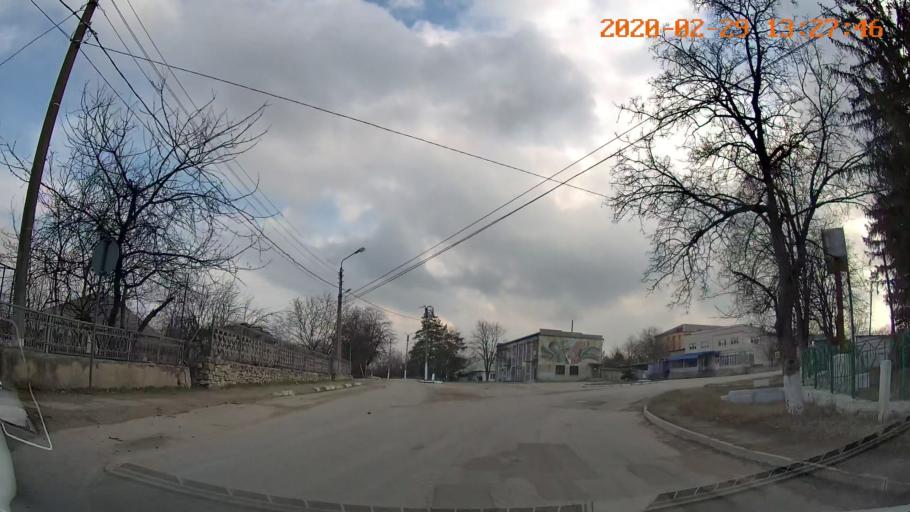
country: MD
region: Telenesti
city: Camenca
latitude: 47.9104
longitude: 28.6448
